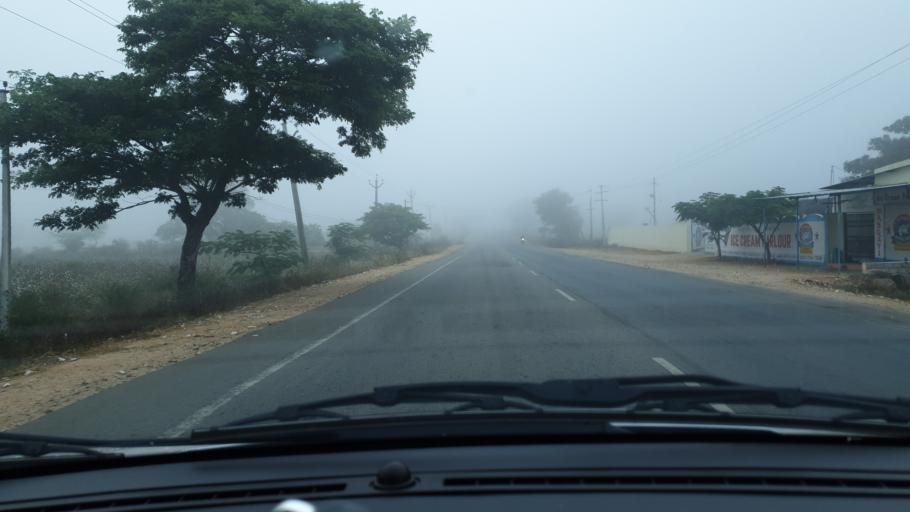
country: IN
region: Telangana
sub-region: Mahbubnagar
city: Nagar Karnul
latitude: 16.6642
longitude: 78.5619
